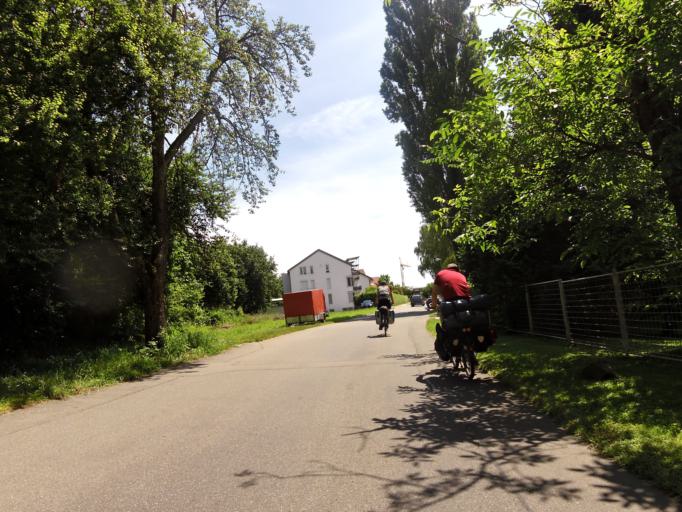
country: DE
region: Baden-Wuerttemberg
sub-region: Tuebingen Region
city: Uberlingen
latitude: 47.7504
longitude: 9.2007
